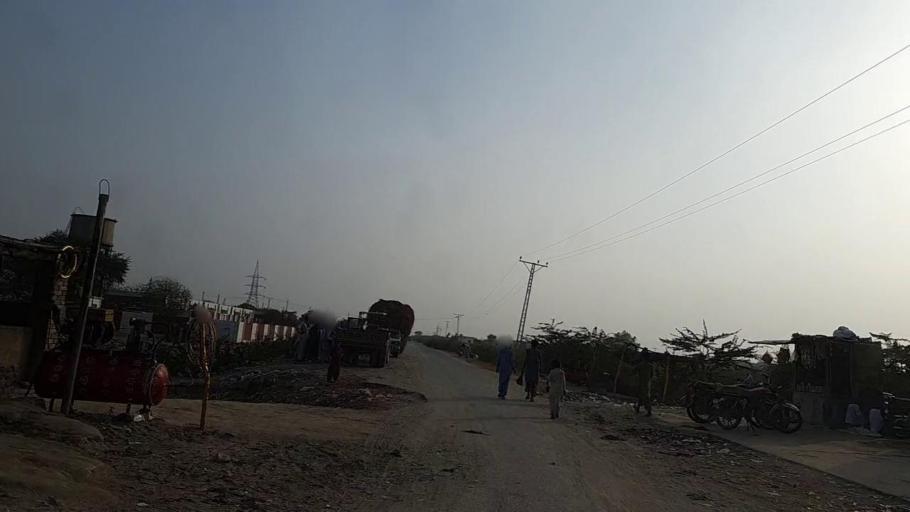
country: PK
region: Sindh
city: Naukot
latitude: 24.6551
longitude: 69.2900
